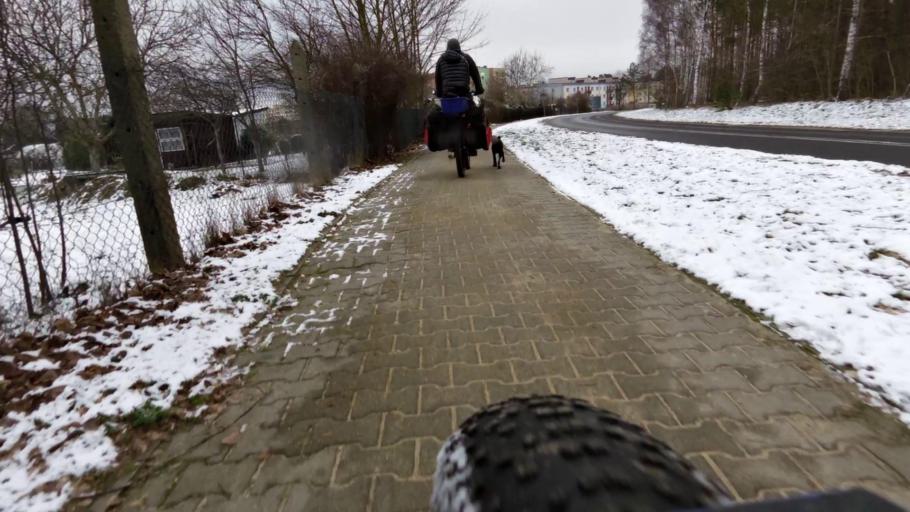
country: PL
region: West Pomeranian Voivodeship
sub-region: Powiat walecki
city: Miroslawiec
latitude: 53.3692
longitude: 16.0845
